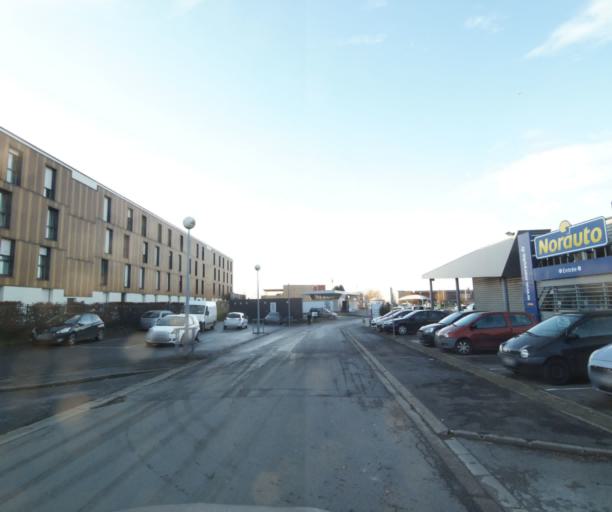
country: FR
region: Nord-Pas-de-Calais
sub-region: Departement du Nord
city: Famars
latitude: 50.3326
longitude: 3.5119
